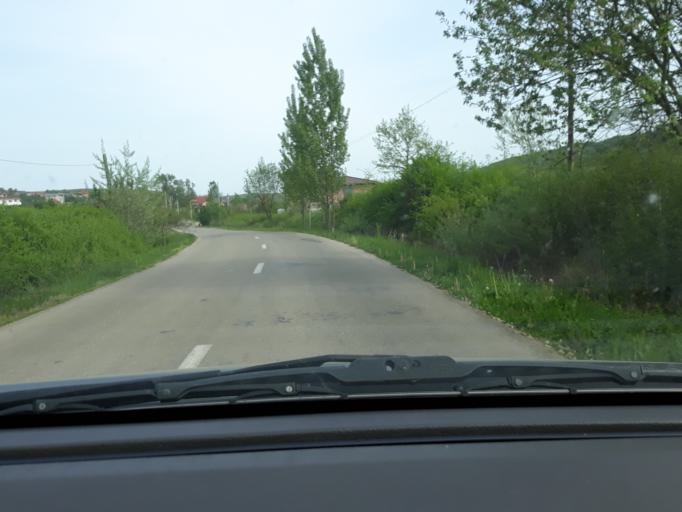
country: RO
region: Bihor
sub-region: Comuna Sanmartin
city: Sanmartin
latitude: 46.9776
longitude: 22.0034
